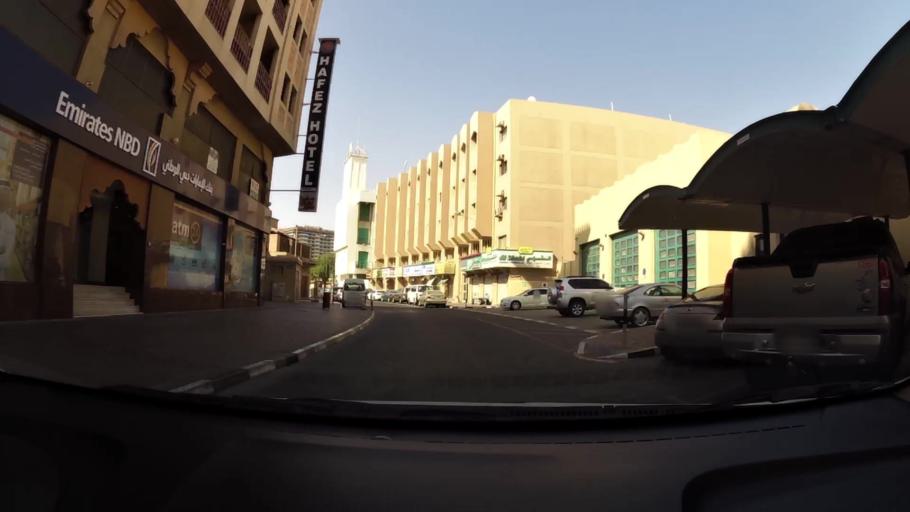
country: AE
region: Ash Shariqah
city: Sharjah
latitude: 25.2678
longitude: 55.2940
